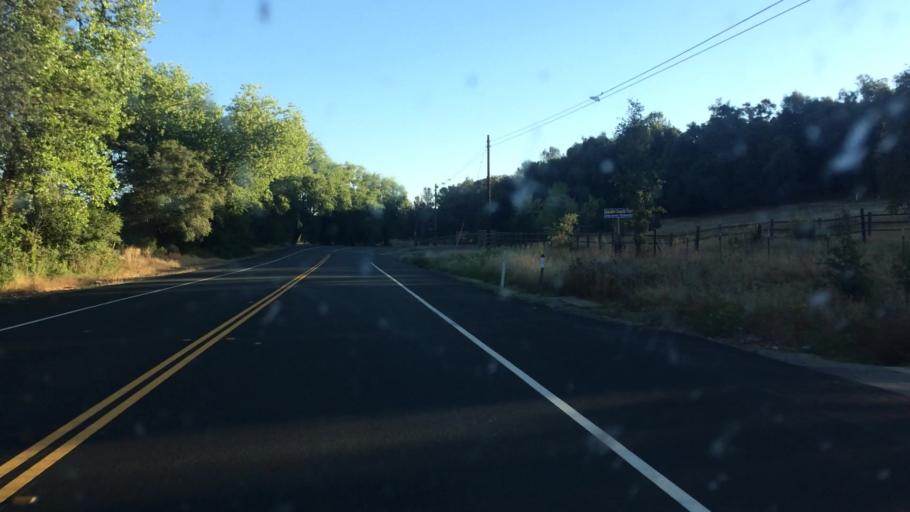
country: US
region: California
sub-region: El Dorado County
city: Deer Park
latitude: 38.6561
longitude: -120.8537
